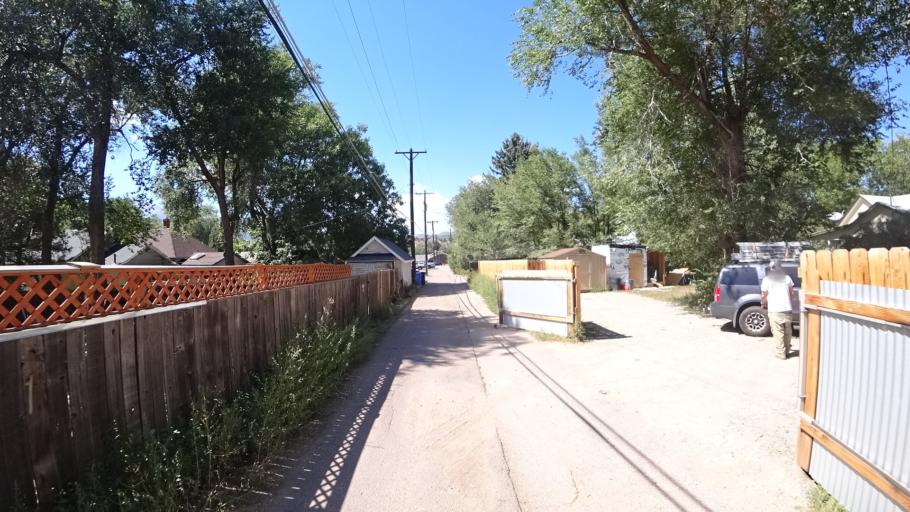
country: US
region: Colorado
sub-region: El Paso County
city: Colorado Springs
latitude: 38.8534
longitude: -104.8666
